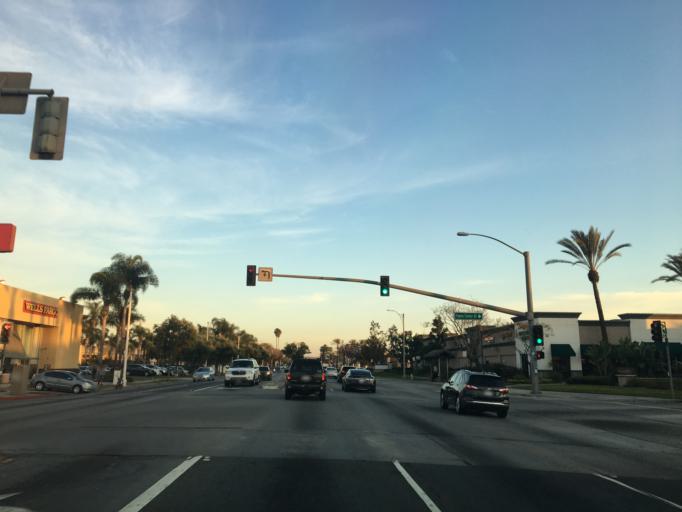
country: US
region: California
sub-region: Los Angeles County
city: Pico Rivera
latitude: 33.9851
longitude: -118.1005
